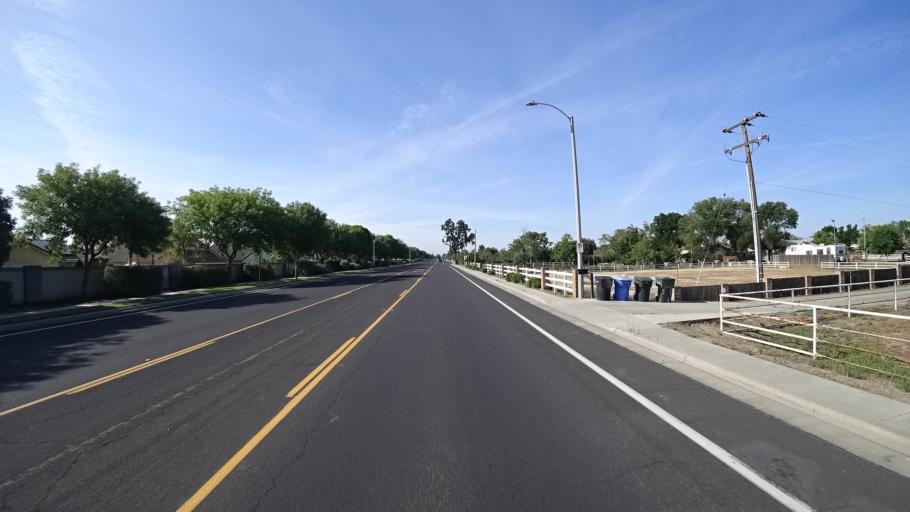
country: US
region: California
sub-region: Kings County
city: Lucerne
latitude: 36.3641
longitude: -119.6371
